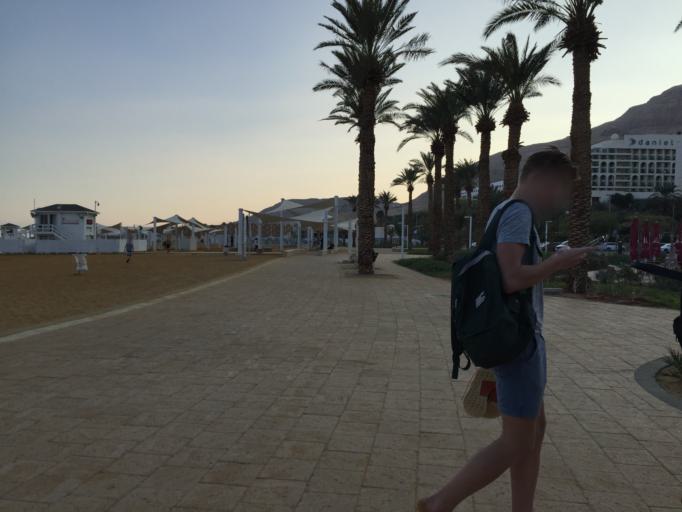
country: IL
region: Southern District
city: `En Boqeq
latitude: 31.1967
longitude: 35.3629
